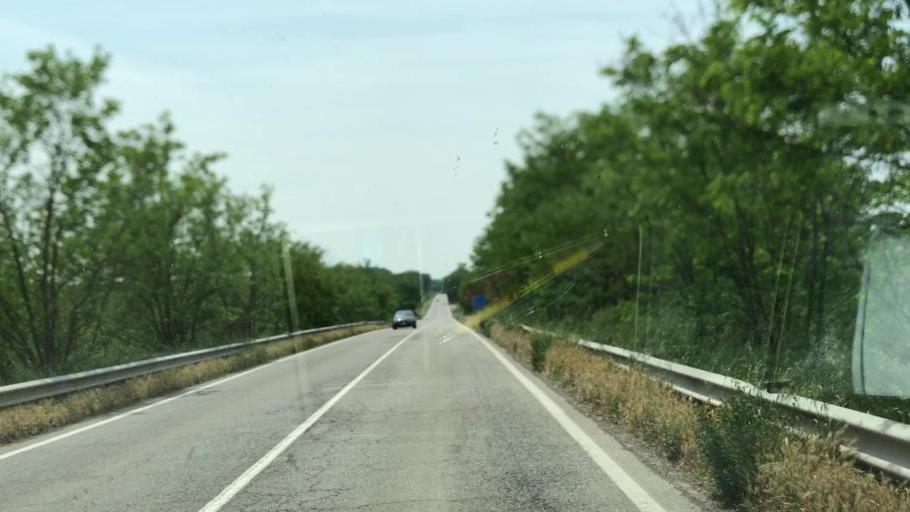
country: IT
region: Lombardy
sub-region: Provincia di Mantova
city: Gazzuolo
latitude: 45.0688
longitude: 10.5866
